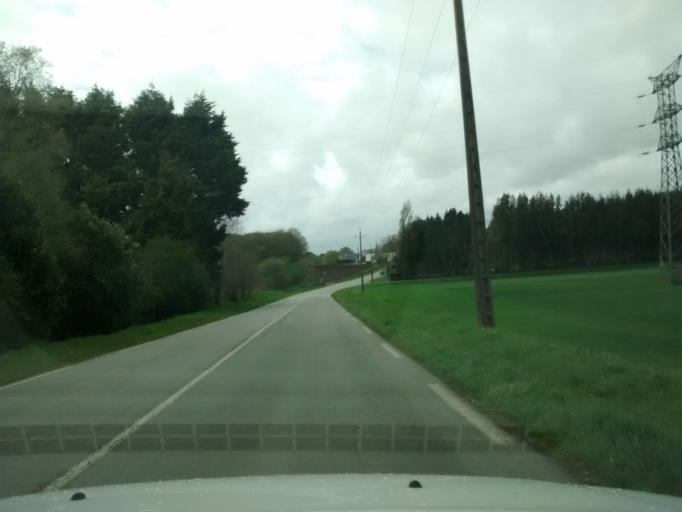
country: FR
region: Brittany
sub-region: Departement du Morbihan
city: Gestel
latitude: 47.7964
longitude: -3.4700
